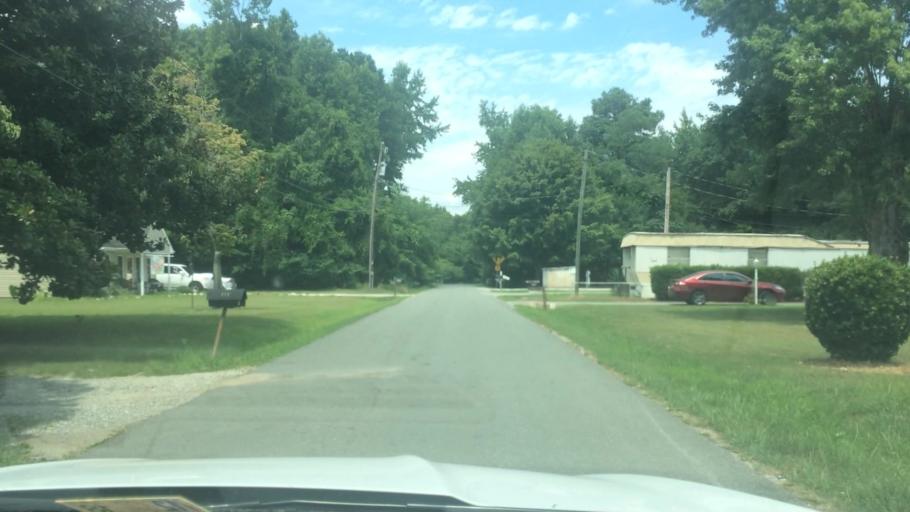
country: US
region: Virginia
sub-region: City of Williamsburg
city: Williamsburg
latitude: 37.2189
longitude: -76.6273
